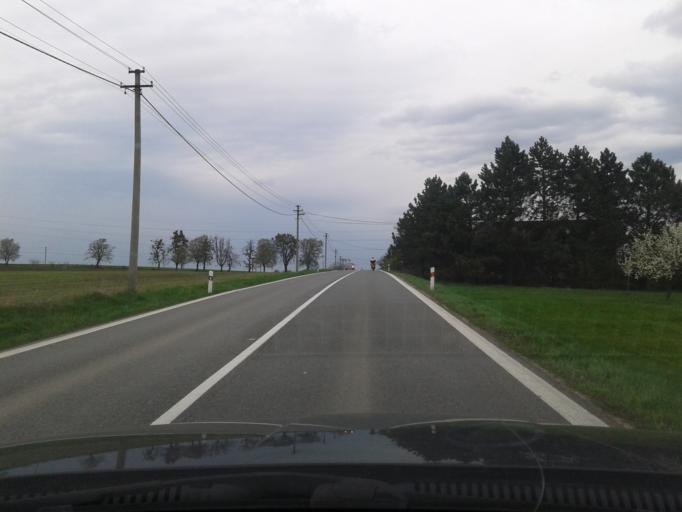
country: CZ
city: Sedliste
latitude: 49.7103
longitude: 18.3679
